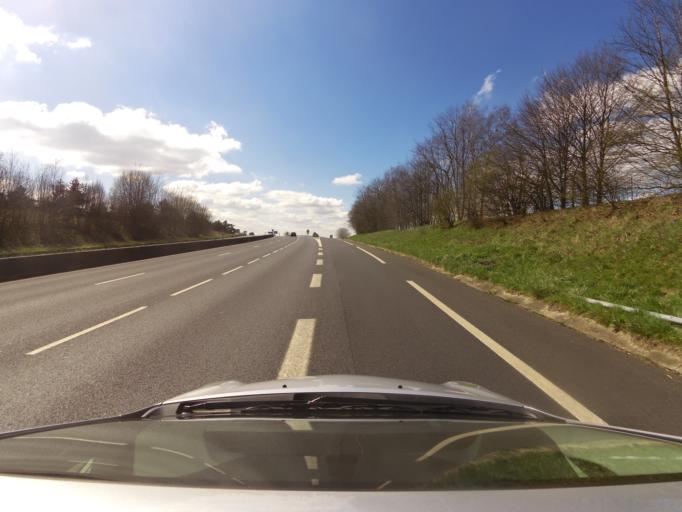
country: FR
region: Haute-Normandie
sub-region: Departement de la Seine-Maritime
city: Saint-Saens
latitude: 49.6565
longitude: 1.2722
